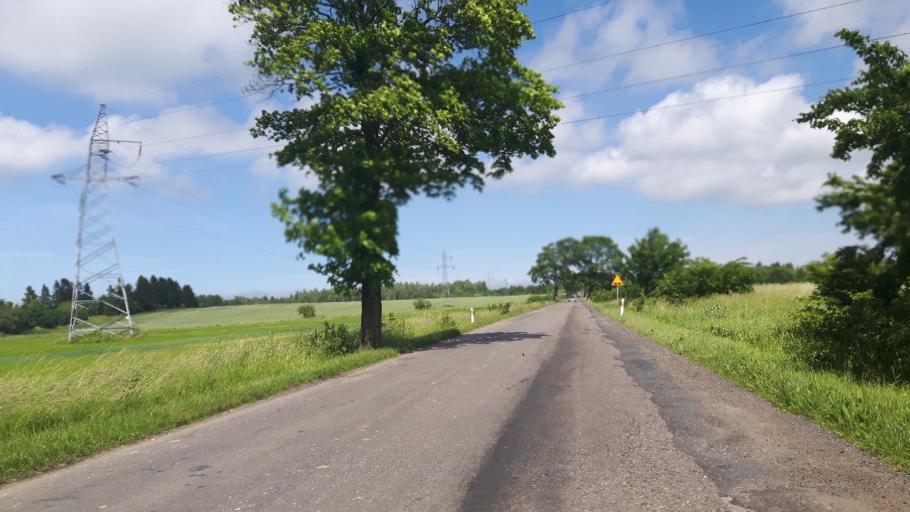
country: PL
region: Pomeranian Voivodeship
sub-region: Powiat slupski
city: Ustka
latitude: 54.5547
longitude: 16.8385
